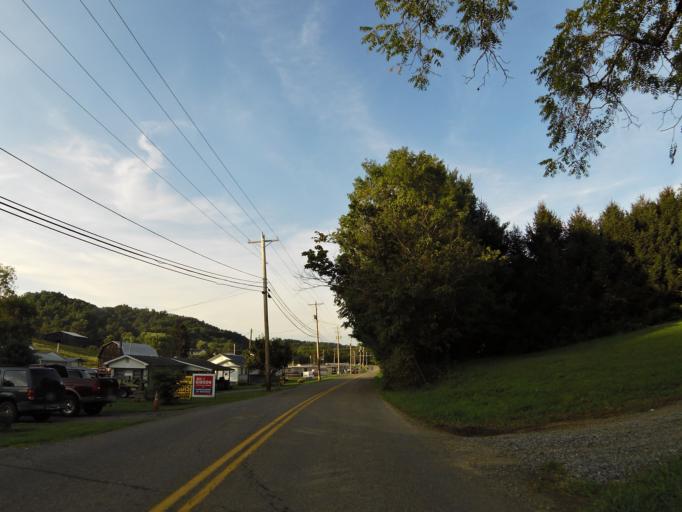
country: US
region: Virginia
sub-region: Washington County
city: Abingdon
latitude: 36.6998
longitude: -81.9163
